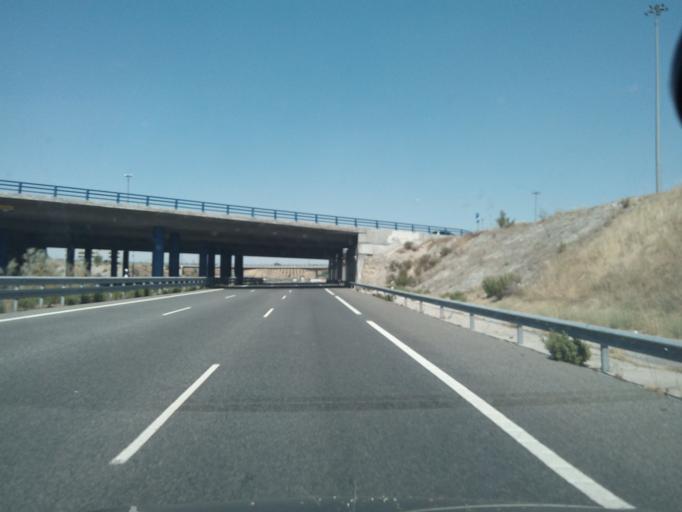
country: ES
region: Madrid
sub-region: Provincia de Madrid
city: Villa de Vallecas
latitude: 40.3593
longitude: -3.5662
